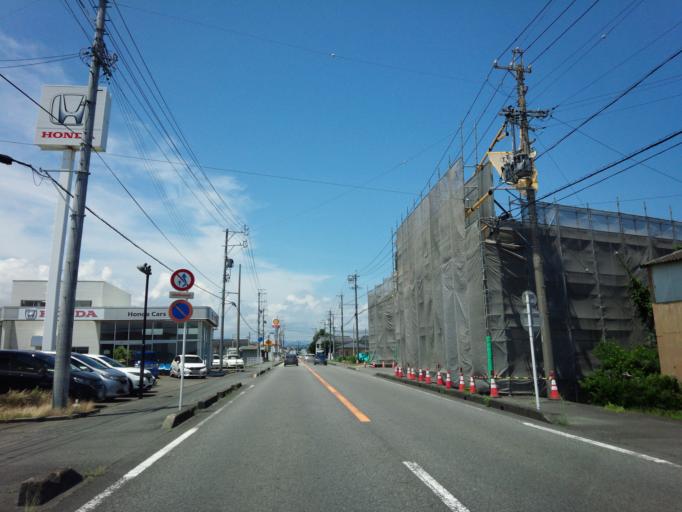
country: JP
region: Shizuoka
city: Shimada
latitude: 34.7895
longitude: 138.2533
